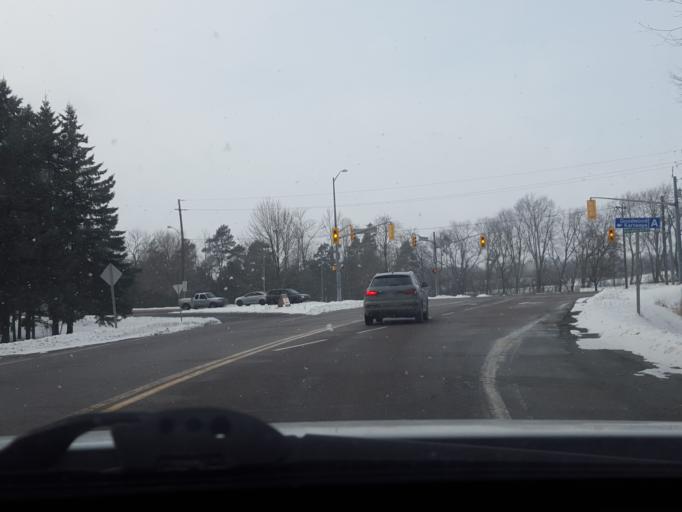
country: CA
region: Ontario
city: Uxbridge
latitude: 44.0334
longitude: -79.2011
